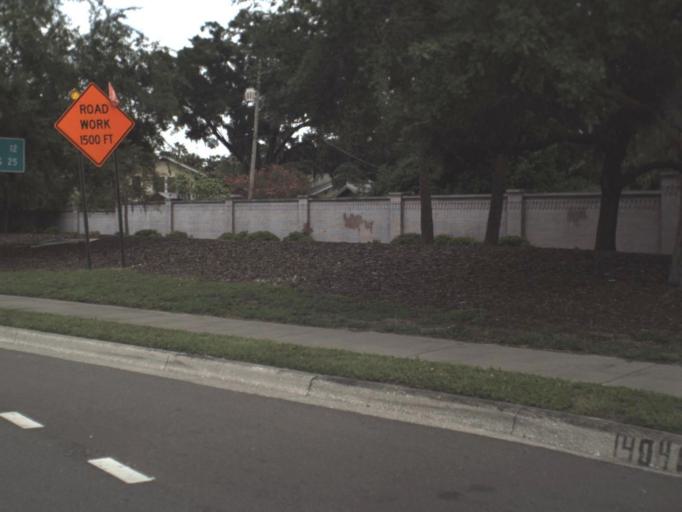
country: US
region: Florida
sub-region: Hillsborough County
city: Tampa
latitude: 27.9963
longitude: -82.4604
